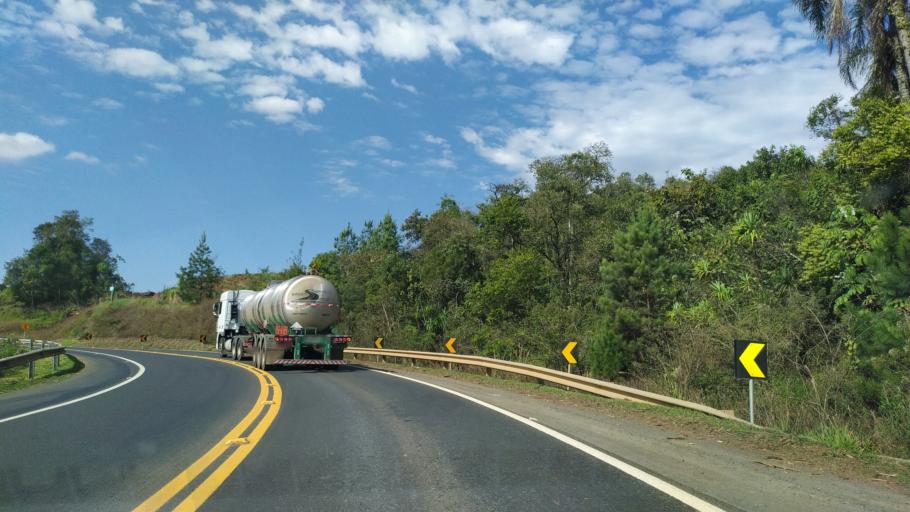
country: BR
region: Parana
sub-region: Telemaco Borba
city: Telemaco Borba
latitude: -24.2712
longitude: -50.7178
